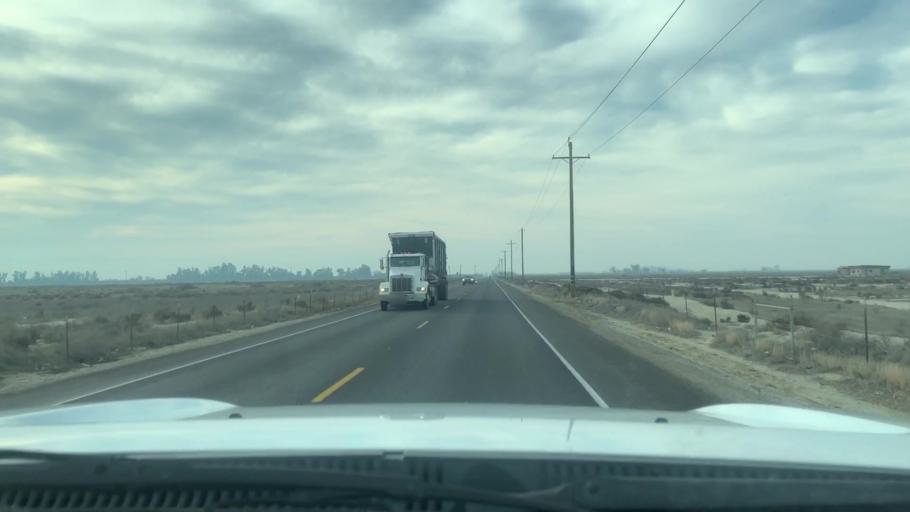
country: US
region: California
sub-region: Kern County
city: Buttonwillow
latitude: 35.4422
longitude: -119.3879
